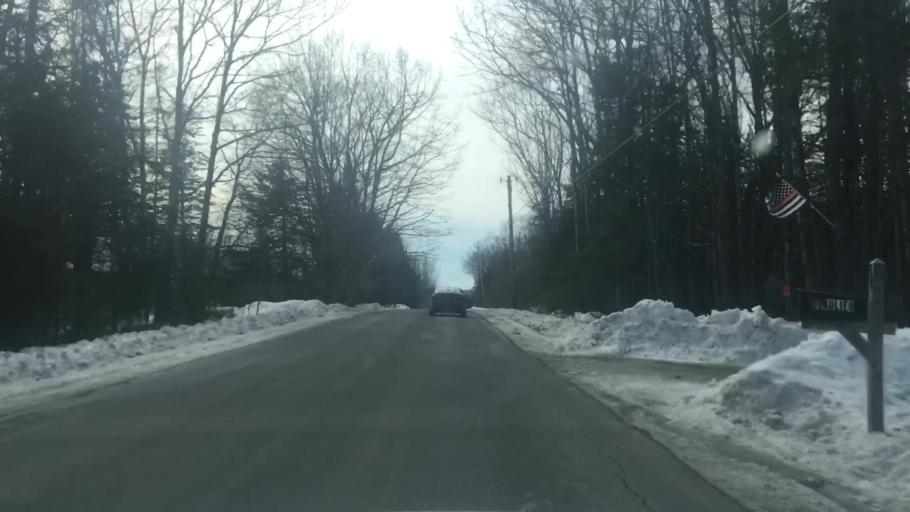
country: US
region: Maine
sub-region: Hancock County
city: Orland
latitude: 44.6007
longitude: -68.7213
